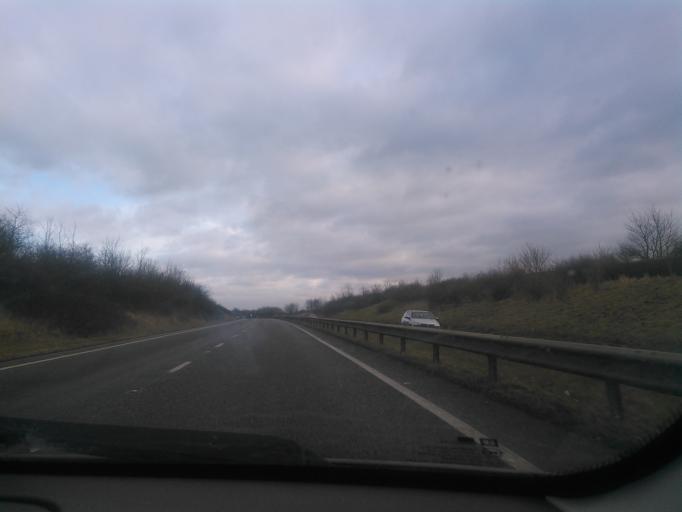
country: GB
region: England
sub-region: Derby
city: Derby
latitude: 52.8633
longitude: -1.4774
